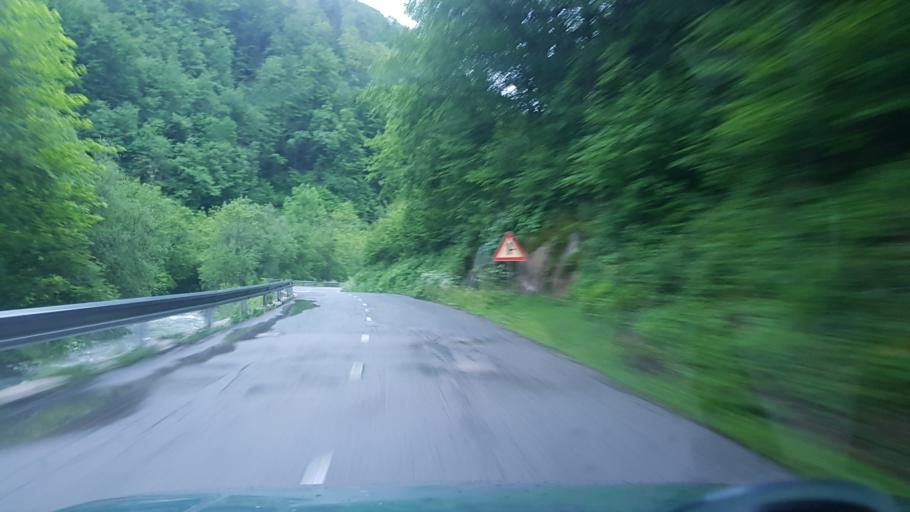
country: SI
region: Cerkno
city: Cerkno
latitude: 46.1873
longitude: 13.9248
